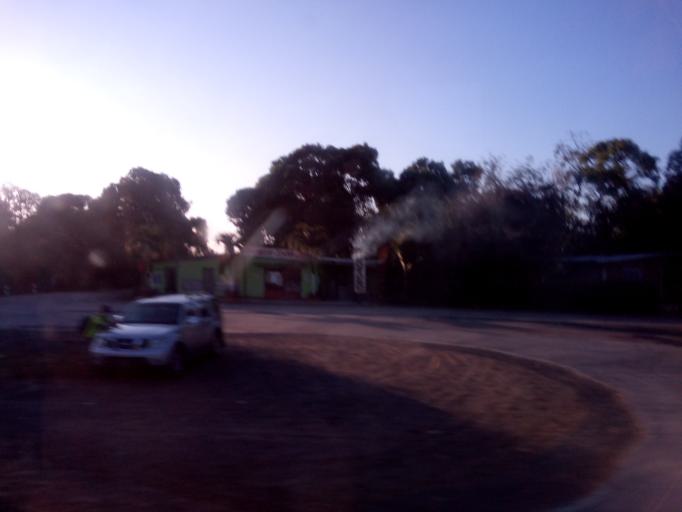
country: PA
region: Veraguas
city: Los Boquerones
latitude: 8.0807
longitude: -80.8970
